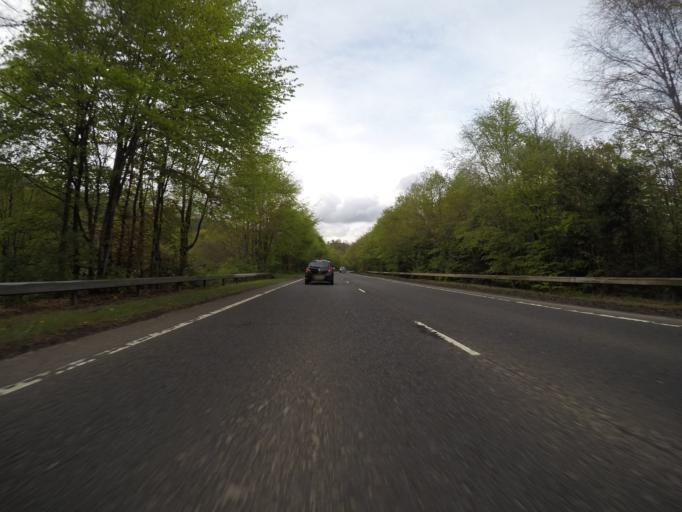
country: GB
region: Scotland
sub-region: West Dunbartonshire
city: Balloch
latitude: 56.0653
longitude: -4.6457
